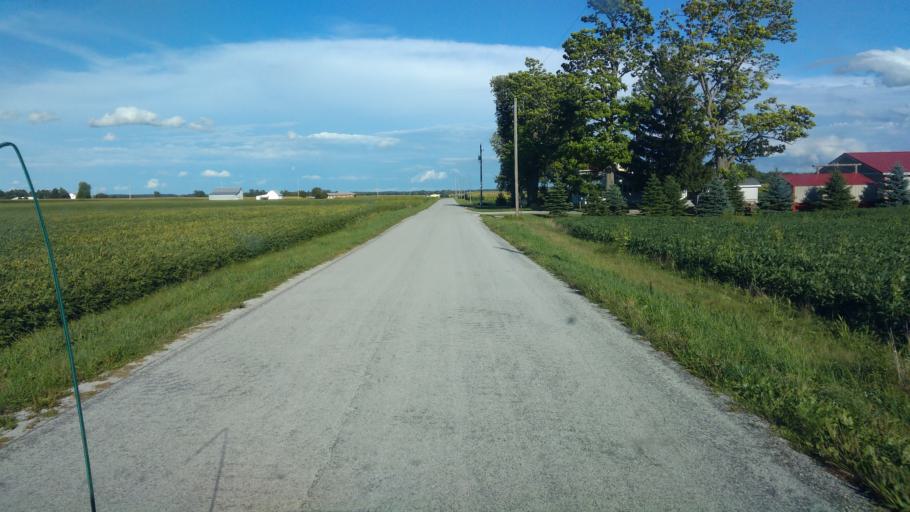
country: US
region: Ohio
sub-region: Hardin County
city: Kenton
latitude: 40.7612
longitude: -83.6595
